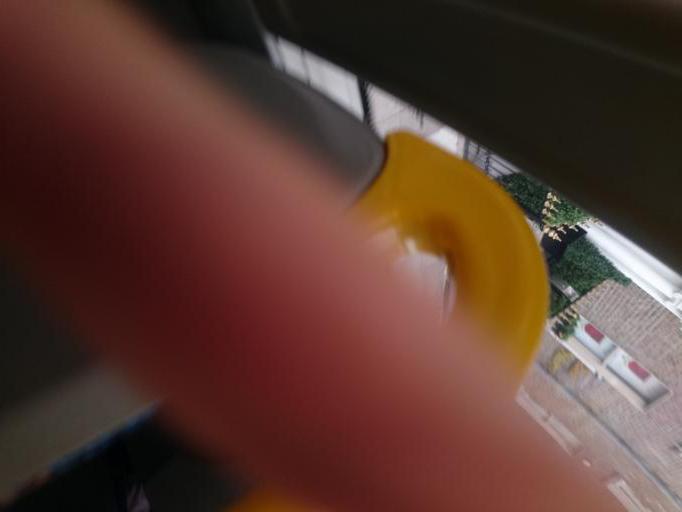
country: IE
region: Leinster
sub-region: Dublin City
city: Dublin
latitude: 53.3339
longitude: -6.2545
